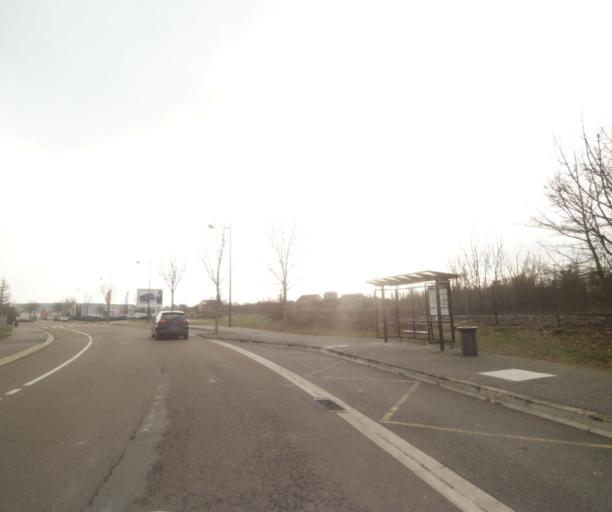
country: FR
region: Champagne-Ardenne
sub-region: Departement de la Haute-Marne
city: Bettancourt-la-Ferree
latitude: 48.6385
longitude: 4.9628
